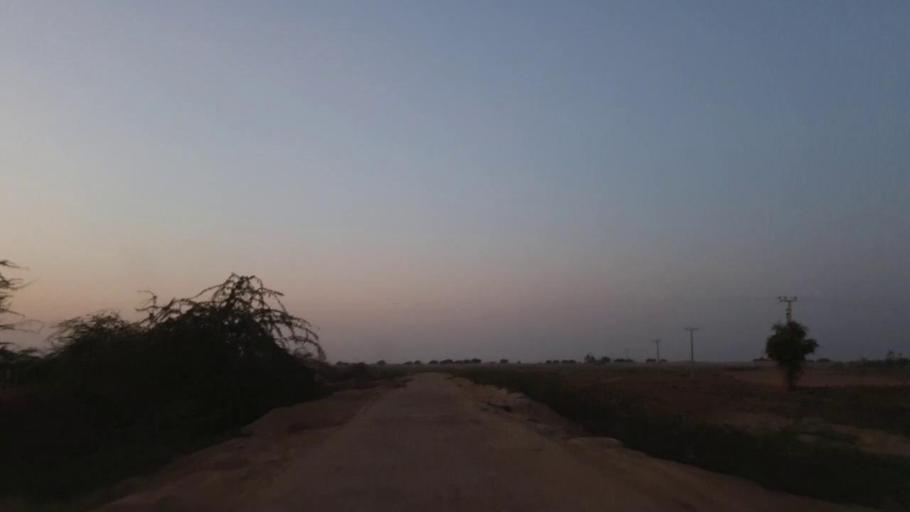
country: PK
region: Sindh
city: Naukot
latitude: 24.9081
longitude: 69.3775
